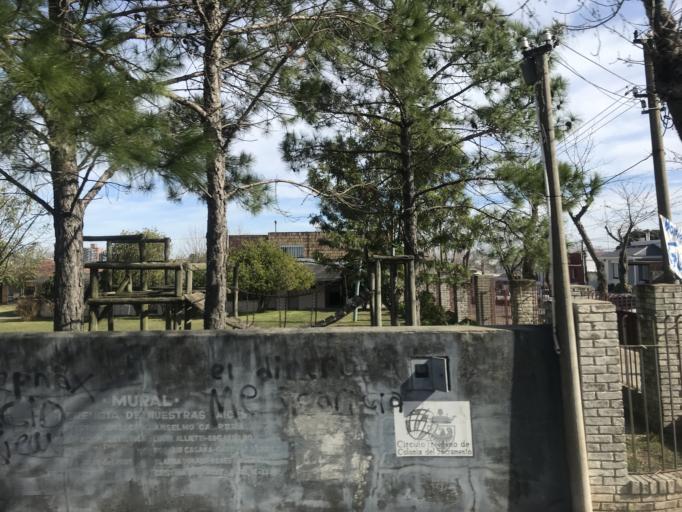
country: UY
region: Colonia
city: Colonia del Sacramento
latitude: -34.4666
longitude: -57.8385
